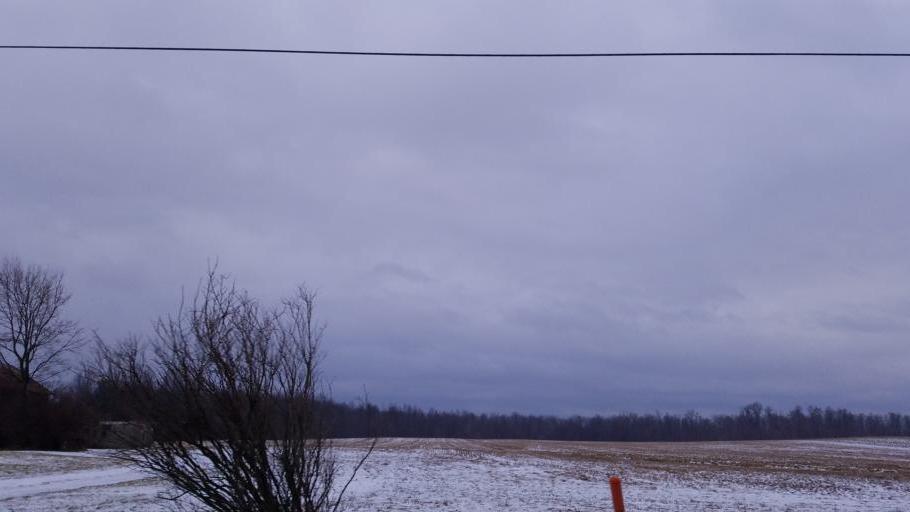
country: US
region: Ohio
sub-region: Richland County
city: Lexington
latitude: 40.6814
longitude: -82.6783
